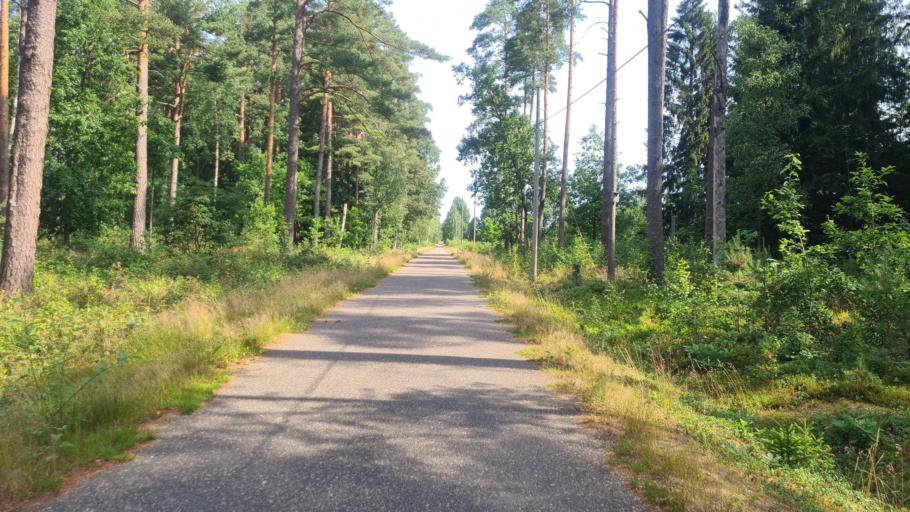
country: SE
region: Kronoberg
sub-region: Ljungby Kommun
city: Ljungby
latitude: 56.8460
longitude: 13.9642
